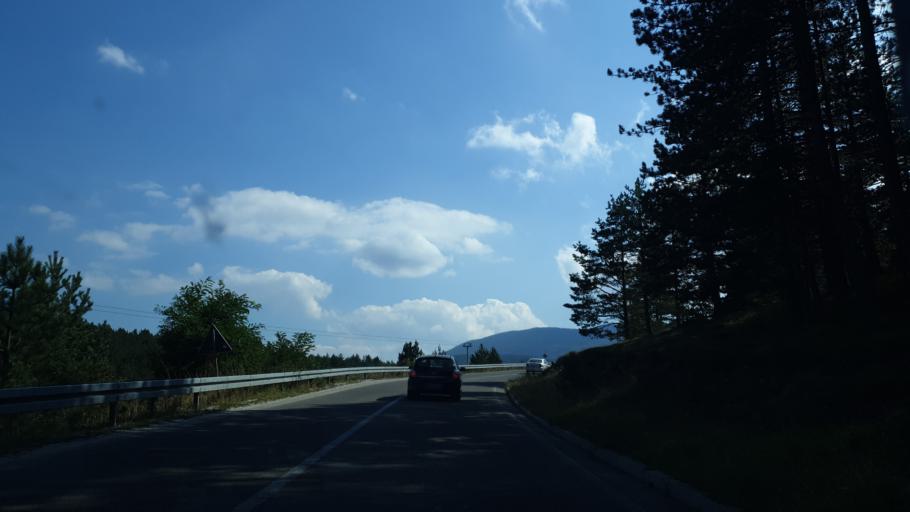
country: RS
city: Zlatibor
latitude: 43.6899
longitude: 19.6636
